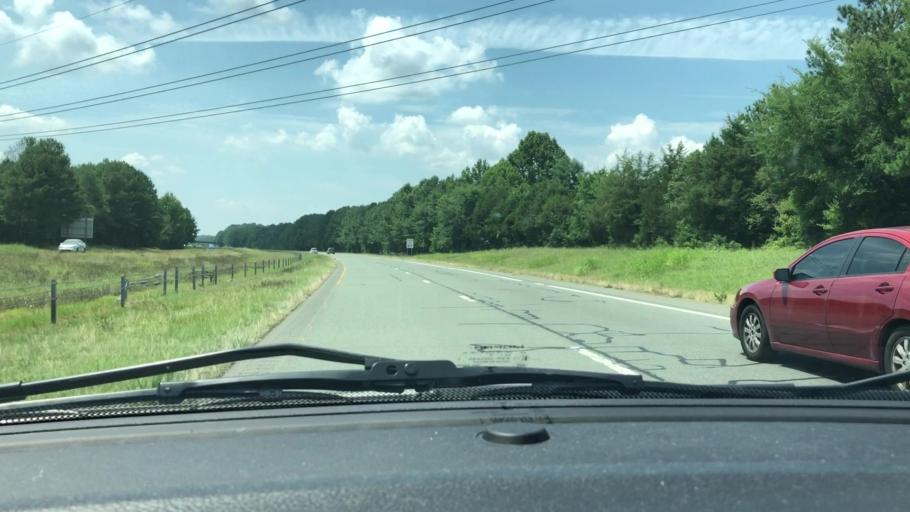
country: US
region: North Carolina
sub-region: Chatham County
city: Siler City
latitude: 35.7427
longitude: -79.4369
